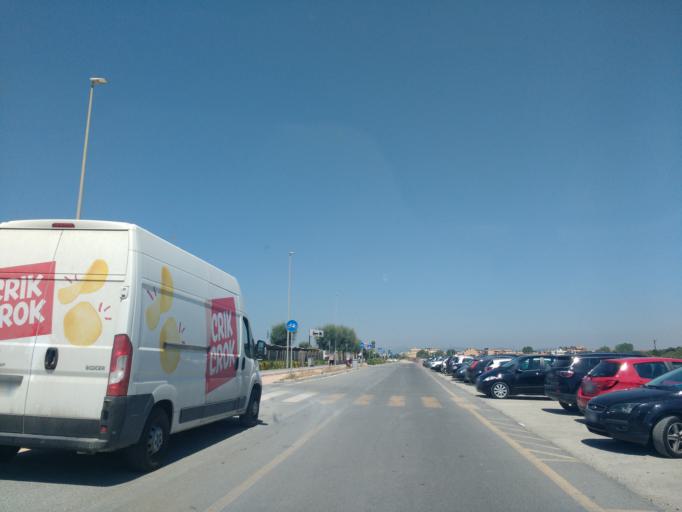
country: IT
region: Latium
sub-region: Citta metropolitana di Roma Capitale
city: Passo Oscuro
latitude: 41.8918
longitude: 12.1655
